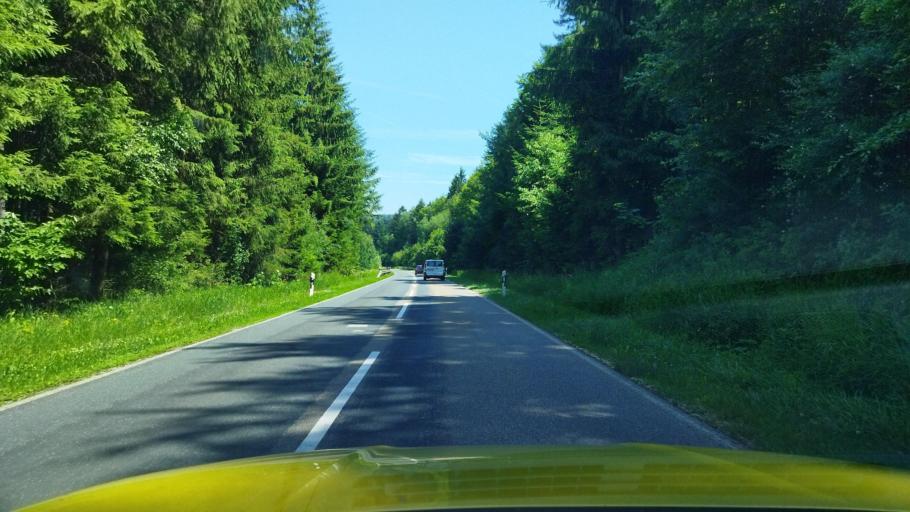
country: DE
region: Bavaria
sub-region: Lower Bavaria
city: Riedenburg
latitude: 48.9448
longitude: 11.6600
